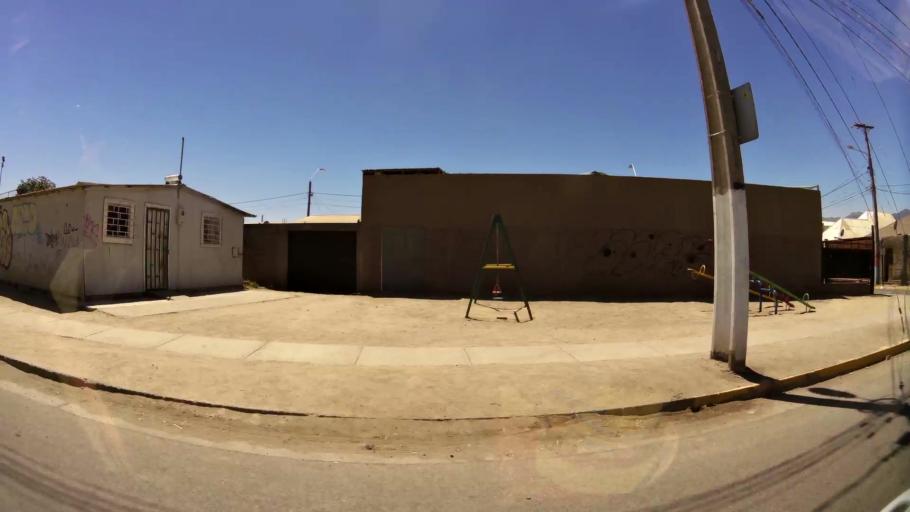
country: CL
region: O'Higgins
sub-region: Provincia de Cachapoal
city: Rancagua
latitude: -34.1652
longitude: -70.6978
